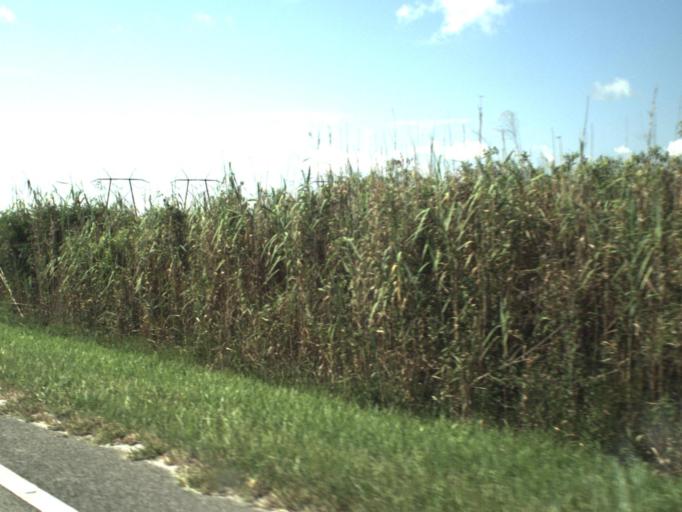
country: US
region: Florida
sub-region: Broward County
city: Weston
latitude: 26.2972
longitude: -80.5090
